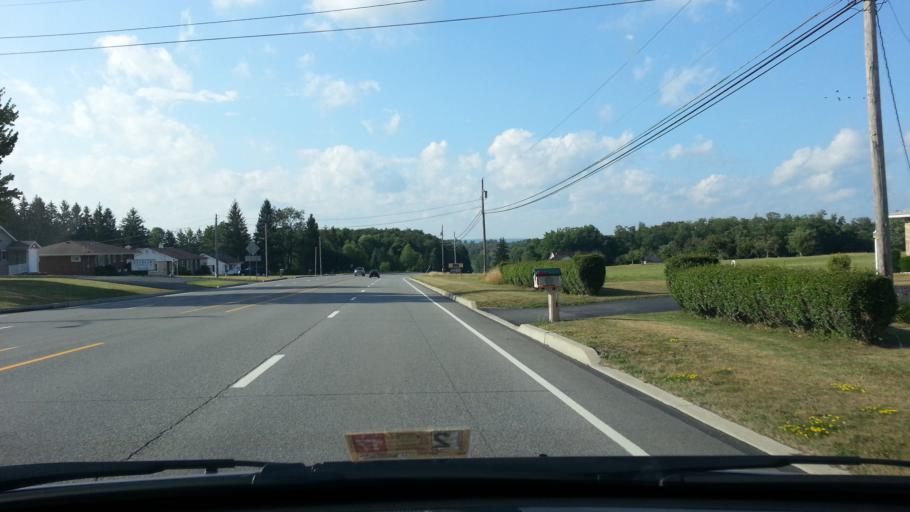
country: US
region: Pennsylvania
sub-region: Elk County
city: Saint Marys
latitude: 41.3770
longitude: -78.5586
